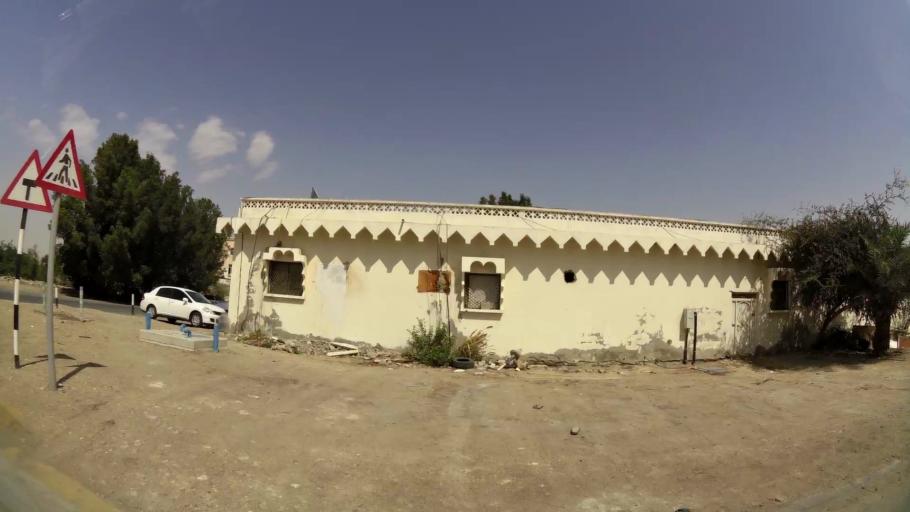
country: AE
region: Abu Dhabi
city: Abu Dhabi
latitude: 24.2885
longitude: 54.6474
